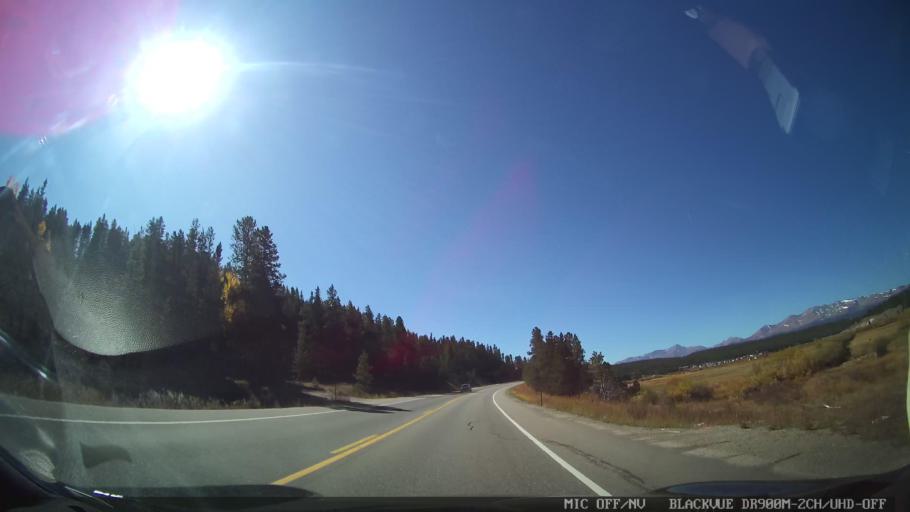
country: US
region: Colorado
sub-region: Lake County
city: Leadville North
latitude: 39.2821
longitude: -106.2805
